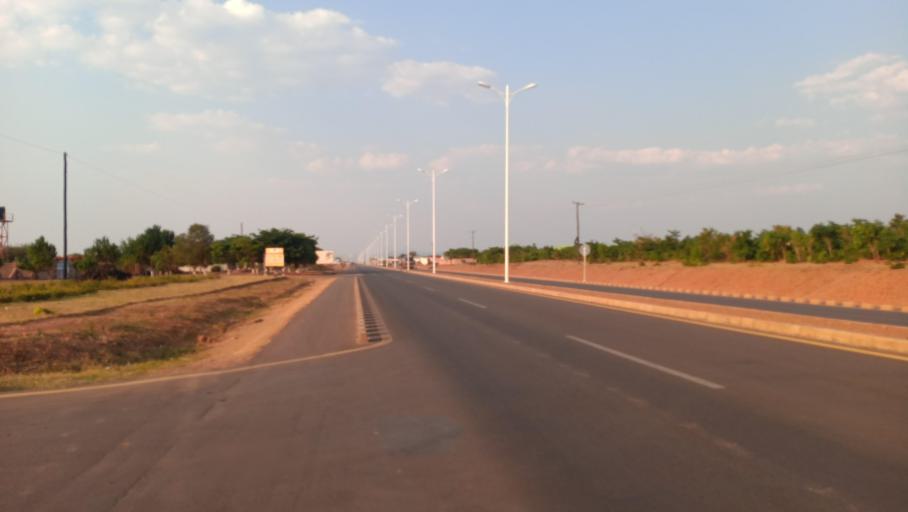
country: ZM
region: Northern
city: Mpika
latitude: -11.8493
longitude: 31.4418
